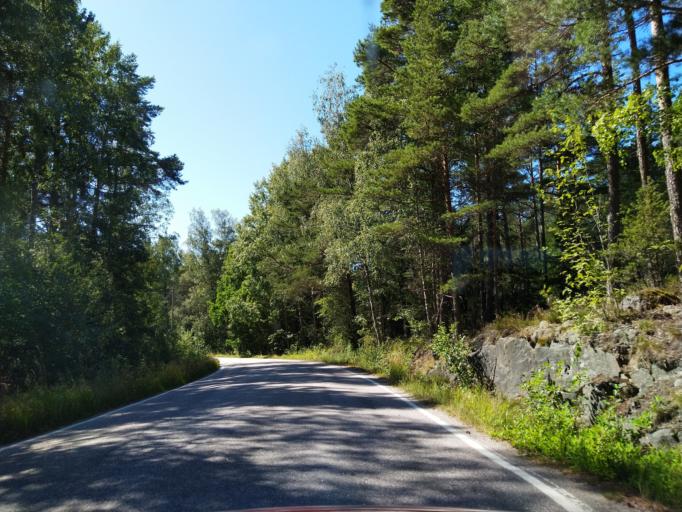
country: FI
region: Varsinais-Suomi
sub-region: Aboland-Turunmaa
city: Dragsfjaerd
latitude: 60.0182
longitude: 22.4791
